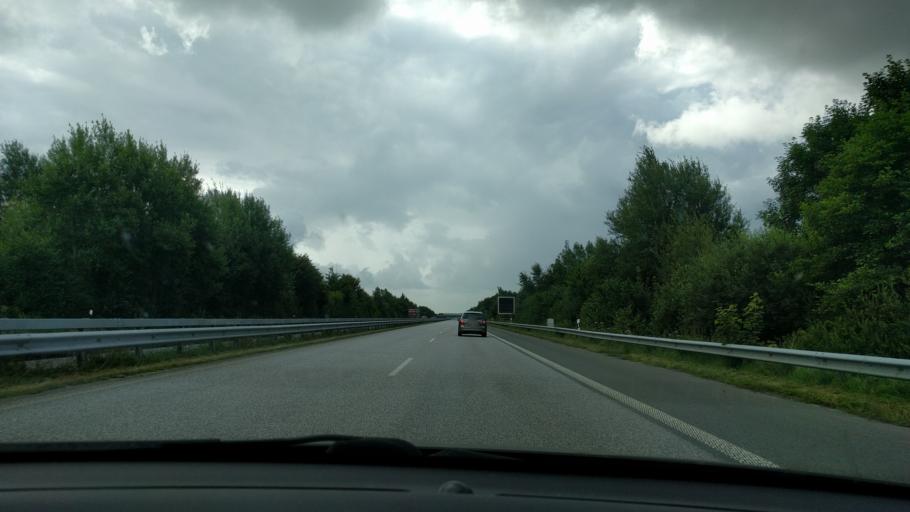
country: DE
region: Schleswig-Holstein
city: Tensbuttel-Rost
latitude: 54.1251
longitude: 9.2559
